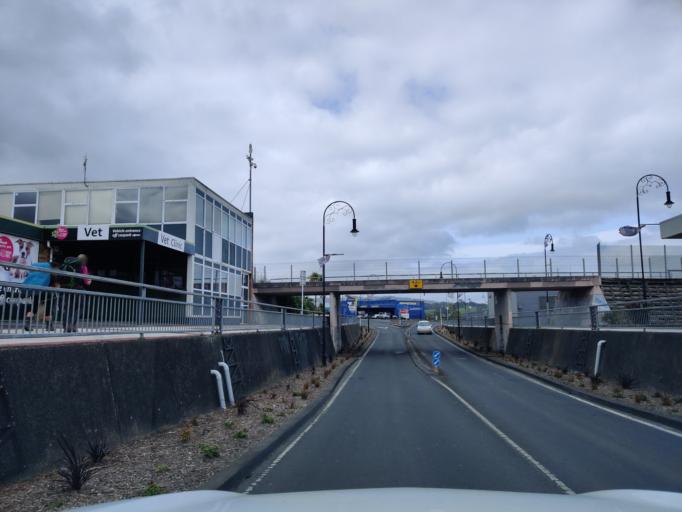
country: NZ
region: Waikato
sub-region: Waikato District
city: Ngaruawahia
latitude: -37.5605
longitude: 175.1587
